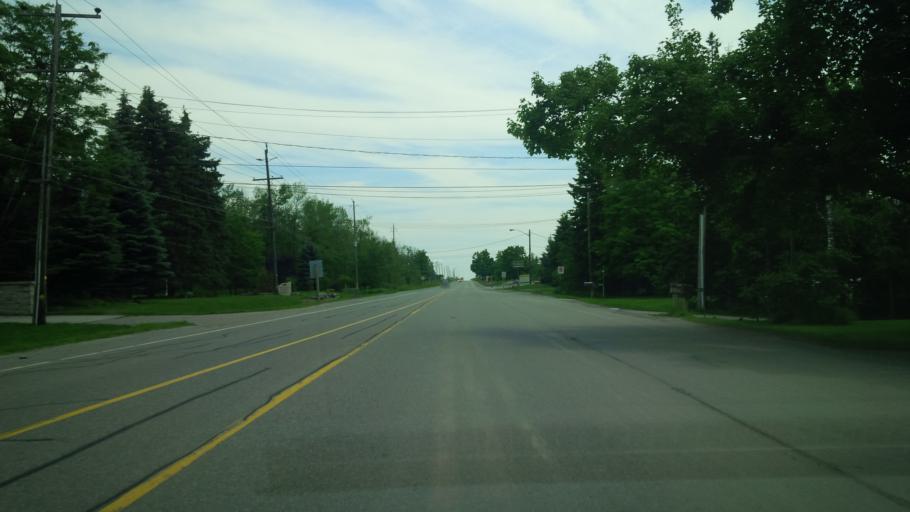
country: CA
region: Ontario
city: Burlington
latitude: 43.4037
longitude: -79.8745
